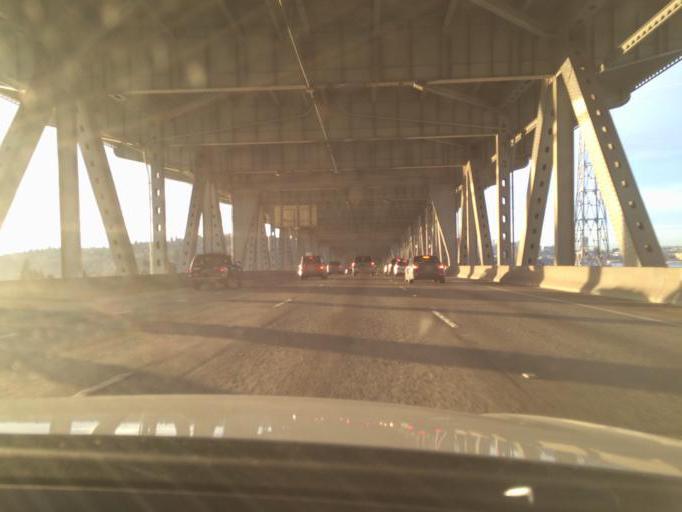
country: US
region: Washington
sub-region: King County
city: Seattle
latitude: 47.6532
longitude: -122.3229
